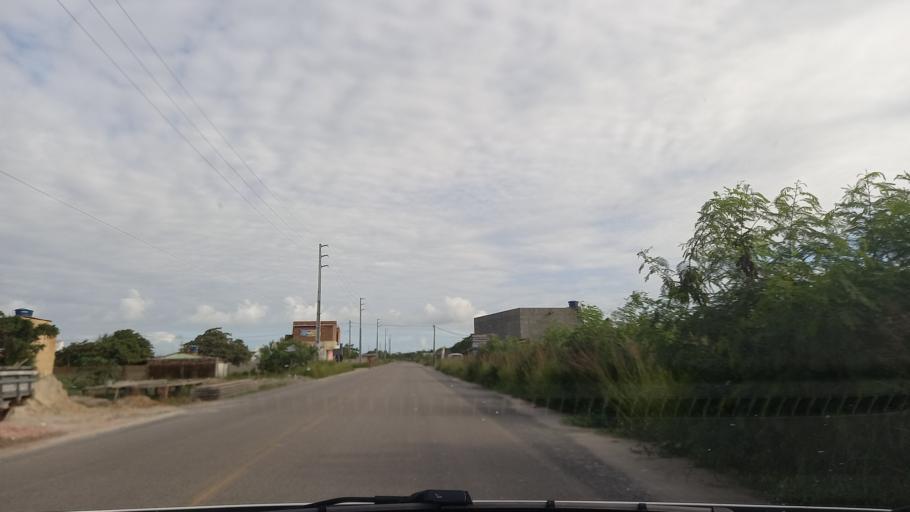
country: BR
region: Pernambuco
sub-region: Tamandare
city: Tamandare
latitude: -8.7312
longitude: -35.0958
